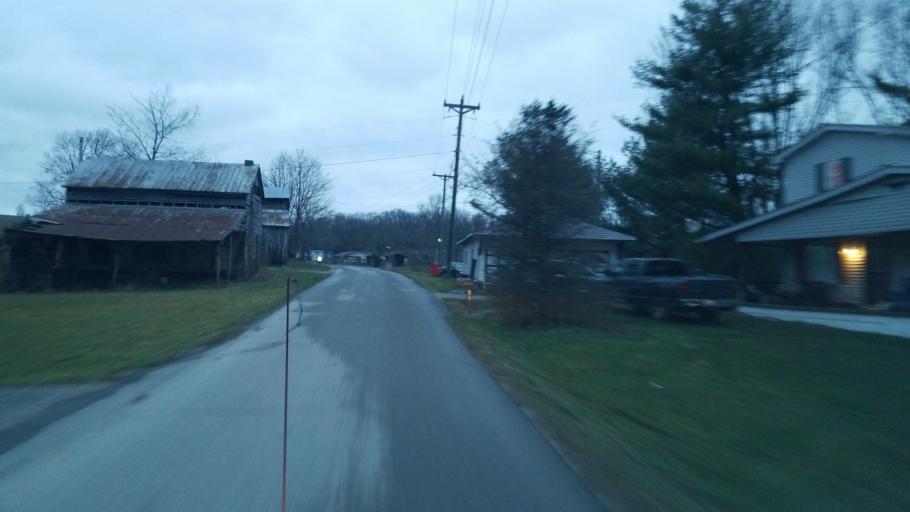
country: US
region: Kentucky
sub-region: Fleming County
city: Flemingsburg
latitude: 38.4983
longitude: -83.6625
